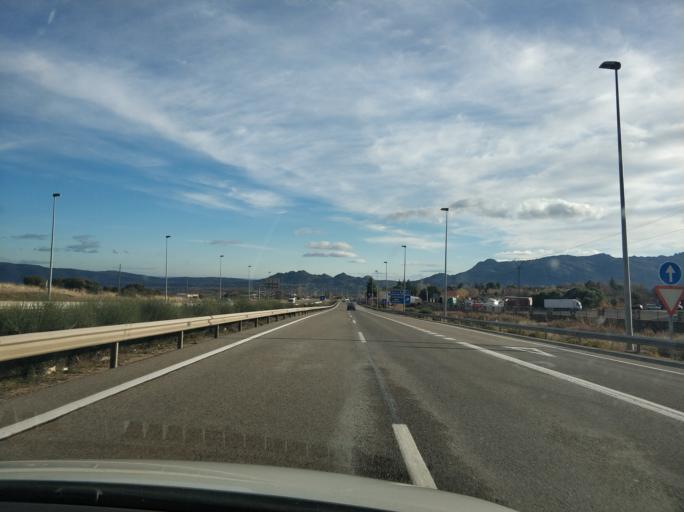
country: ES
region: Madrid
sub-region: Provincia de Madrid
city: Buitrago del Lozoya
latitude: 40.9401
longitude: -3.6302
